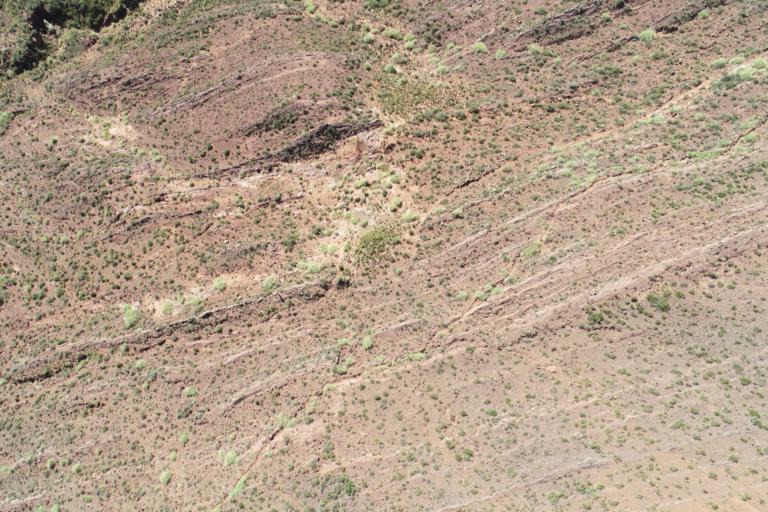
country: BO
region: La Paz
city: Tiahuanaco
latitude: -16.6049
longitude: -68.7599
